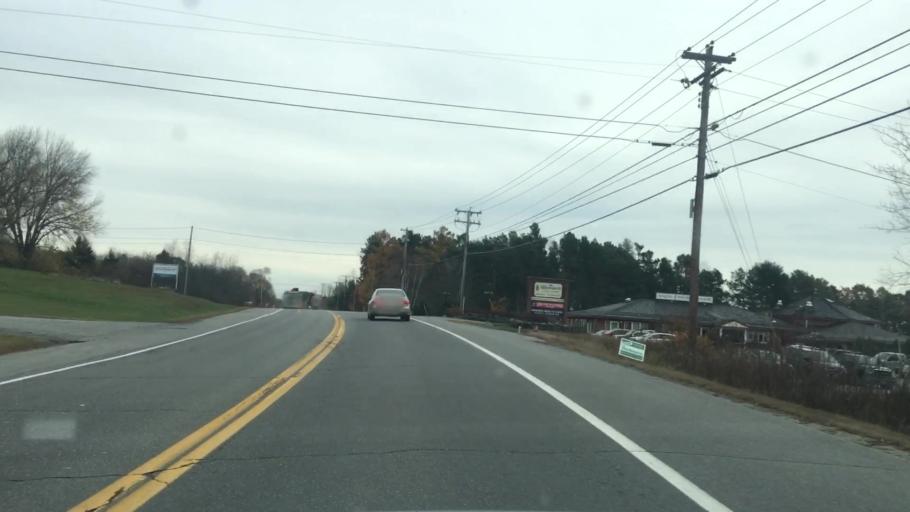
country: US
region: Maine
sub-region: Waldo County
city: Belfast
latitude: 44.4286
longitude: -68.9823
